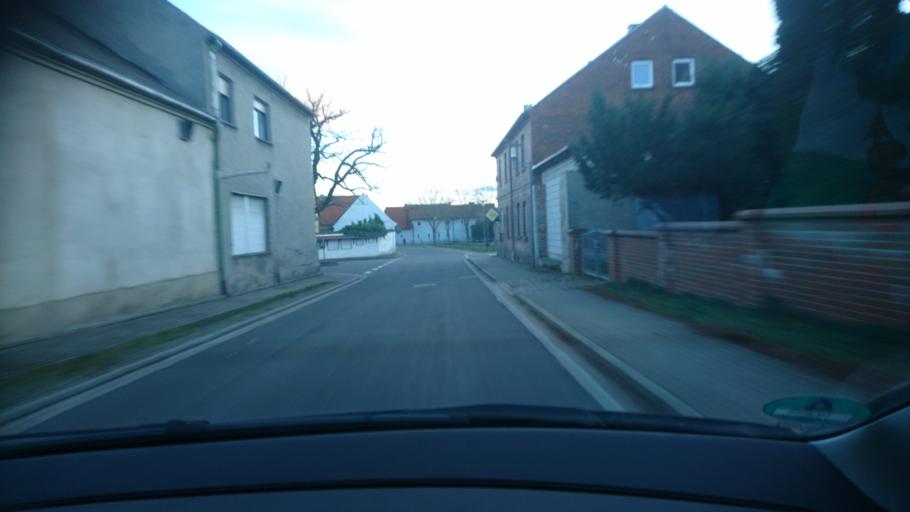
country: DE
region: Saxony
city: Kossa
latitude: 51.5928
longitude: 12.6786
